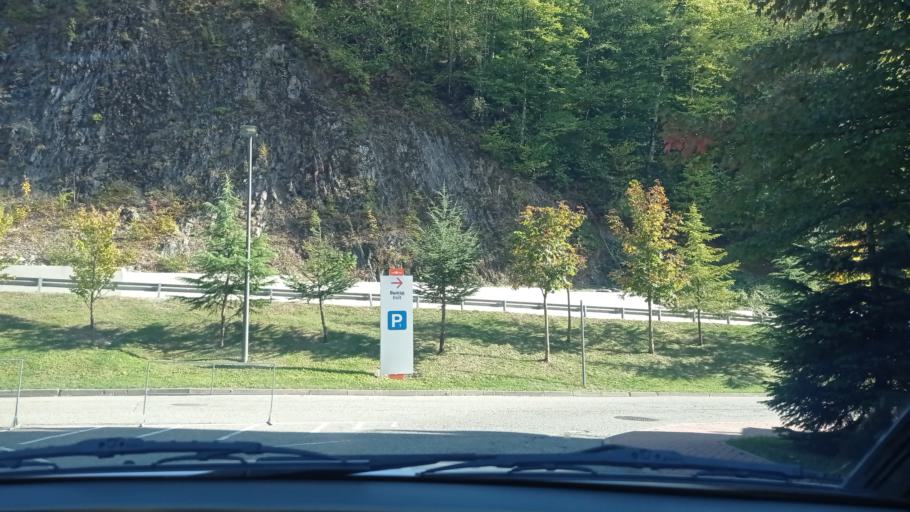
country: RU
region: Krasnodarskiy
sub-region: Sochi City
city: Krasnaya Polyana
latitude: 43.6725
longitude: 40.2990
